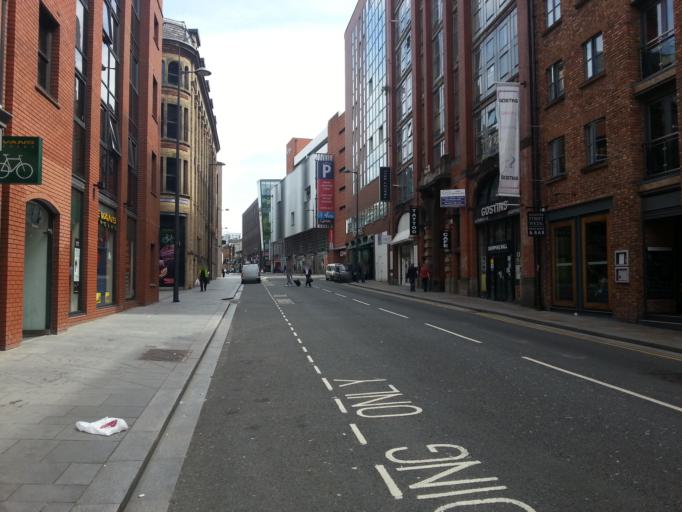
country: GB
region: England
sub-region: Liverpool
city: Liverpool
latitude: 53.4028
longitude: -2.9851
